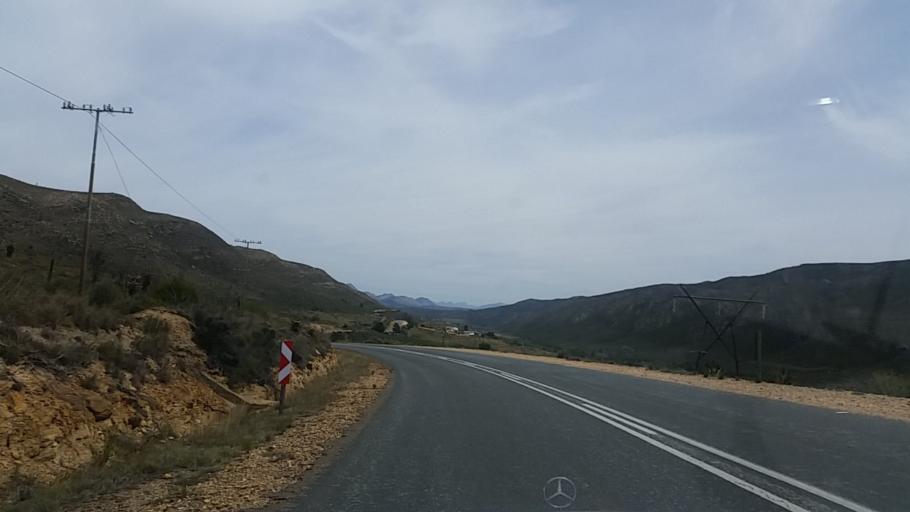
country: ZA
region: Western Cape
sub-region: Eden District Municipality
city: Knysna
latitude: -33.7421
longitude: 23.0021
